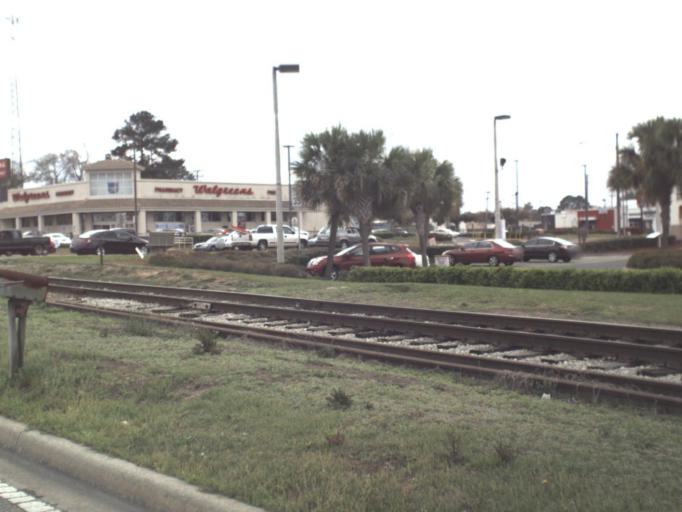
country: US
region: Florida
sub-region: Gadsden County
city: Quincy
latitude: 30.5885
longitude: -84.5911
